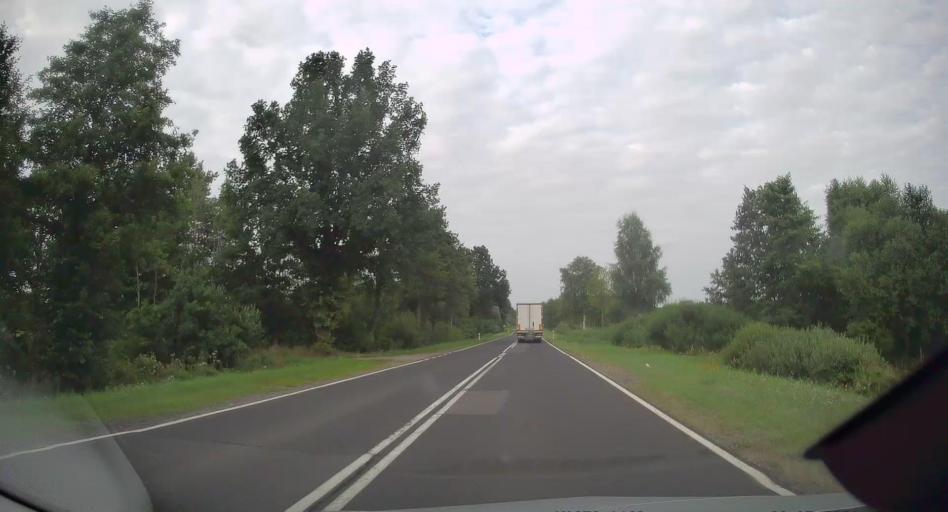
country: PL
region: Lodz Voivodeship
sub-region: Powiat radomszczanski
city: Plawno
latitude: 51.0167
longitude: 19.4240
